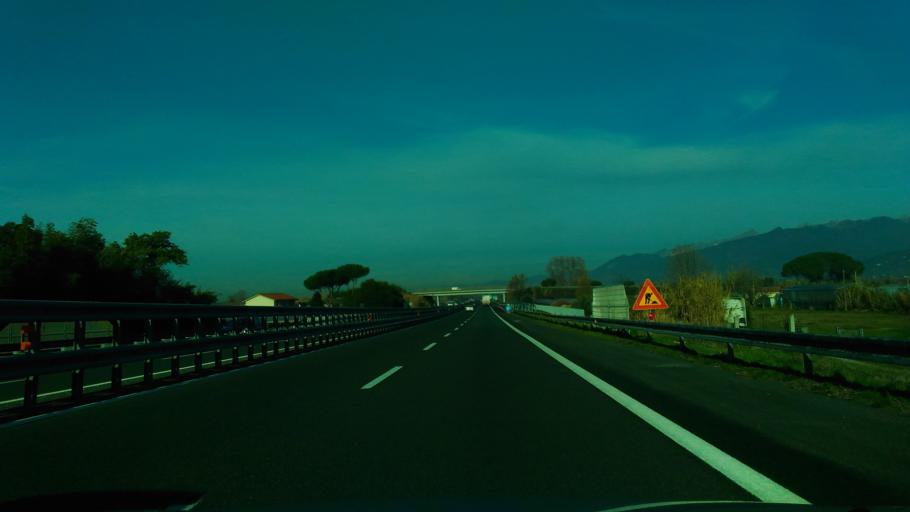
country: IT
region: Tuscany
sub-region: Provincia di Lucca
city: Camaiore
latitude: 43.9124
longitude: 10.2384
